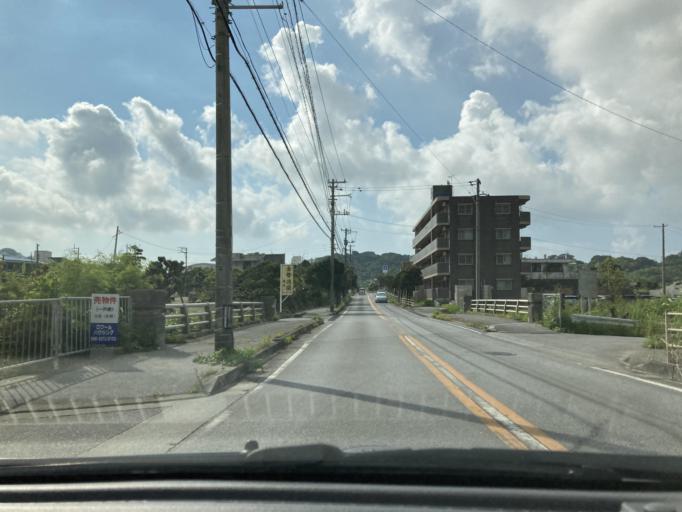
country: JP
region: Okinawa
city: Tomigusuku
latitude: 26.1554
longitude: 127.7497
